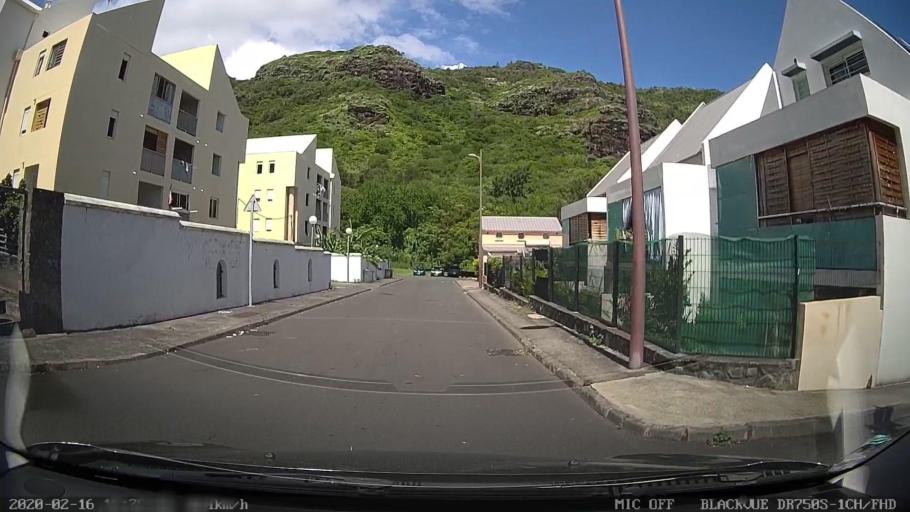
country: RE
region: Reunion
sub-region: Reunion
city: Saint-Denis
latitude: -20.8812
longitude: 55.4405
